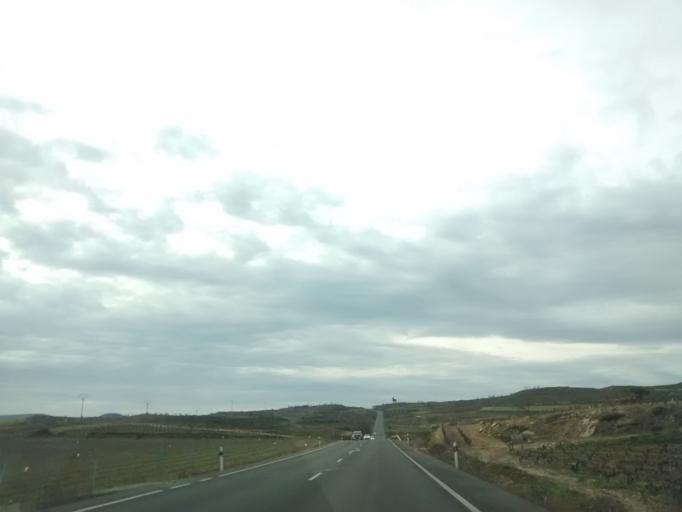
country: ES
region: La Rioja
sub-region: Provincia de La Rioja
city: Torremontalbo
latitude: 42.5083
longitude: -2.7039
